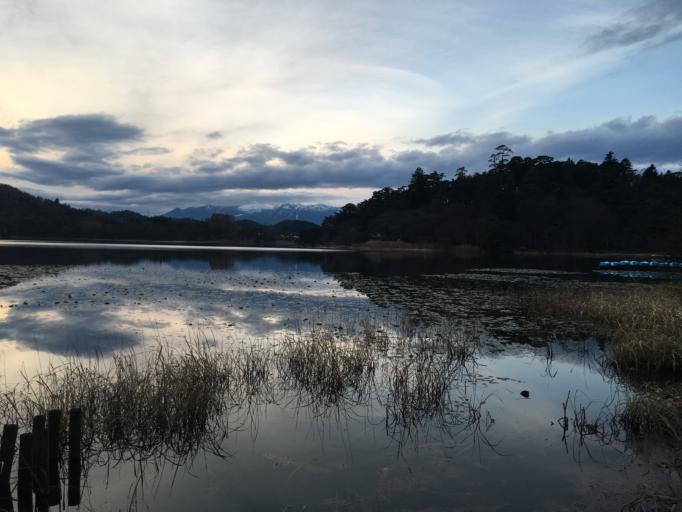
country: JP
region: Tochigi
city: Kuroiso
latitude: 37.1094
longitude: 140.2204
